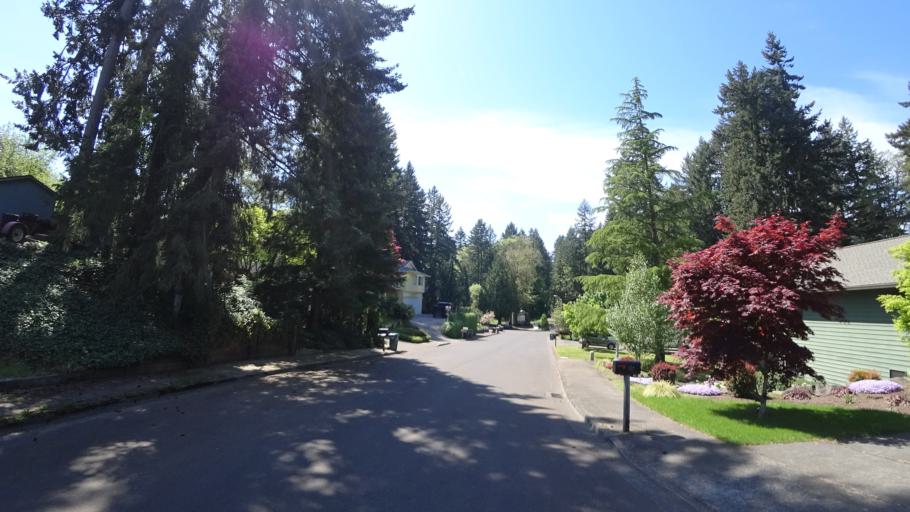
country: US
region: Oregon
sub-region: Washington County
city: Hillsboro
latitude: 45.5177
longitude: -122.9528
